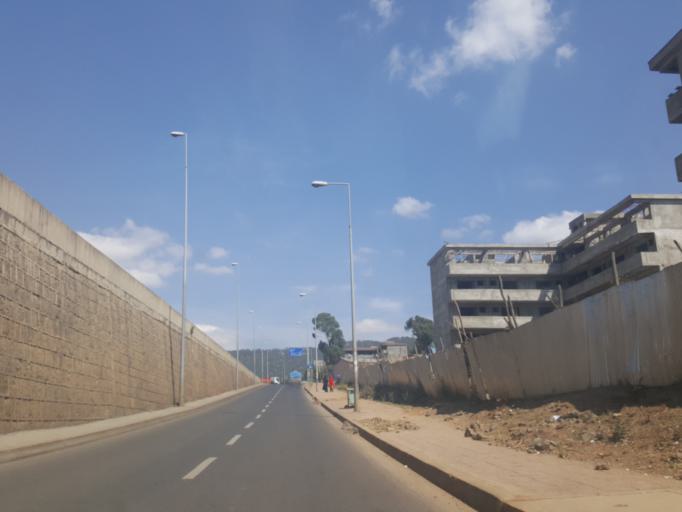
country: ET
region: Adis Abeba
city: Addis Ababa
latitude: 9.0604
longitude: 38.7146
